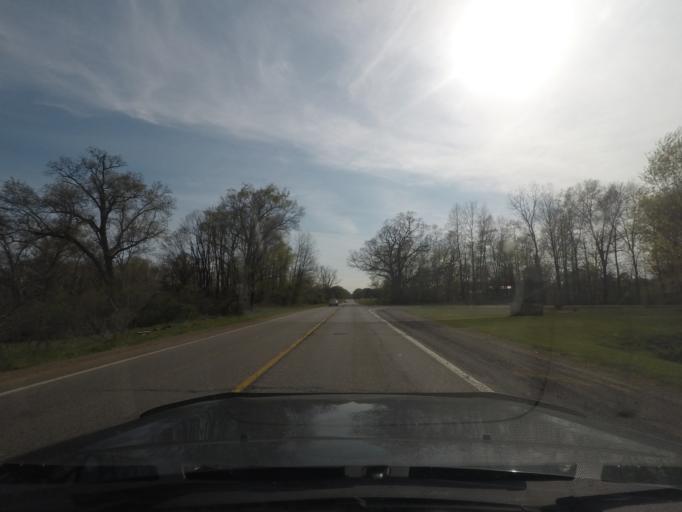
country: US
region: Michigan
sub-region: Berrien County
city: Buchanan
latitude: 41.8004
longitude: -86.4079
